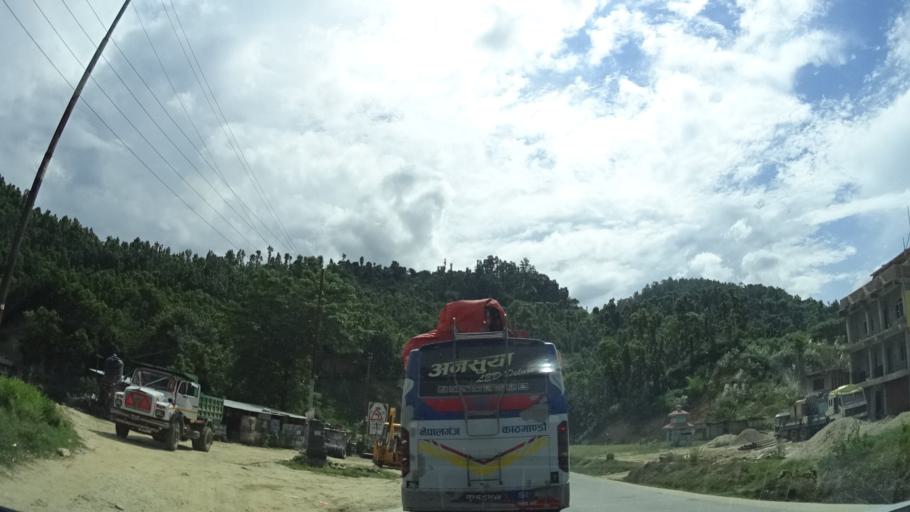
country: NP
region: Central Region
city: Kirtipur
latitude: 27.8039
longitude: 84.9060
